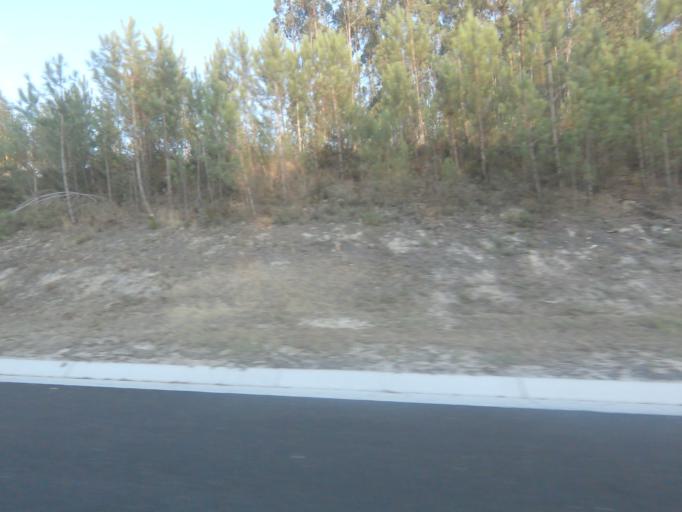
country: PT
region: Leiria
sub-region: Leiria
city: Caranguejeira
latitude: 39.7790
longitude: -8.7394
